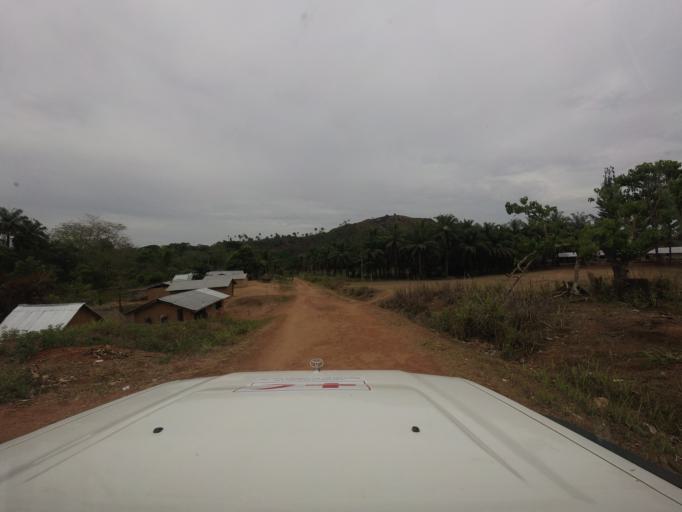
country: SL
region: Eastern Province
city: Buedu
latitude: 8.2747
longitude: -10.2783
